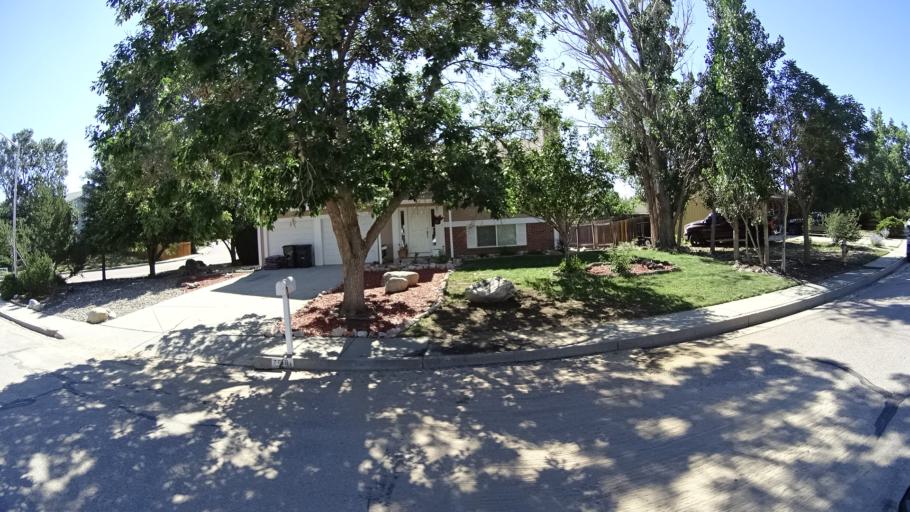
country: US
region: Colorado
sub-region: El Paso County
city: Air Force Academy
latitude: 38.9416
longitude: -104.7866
